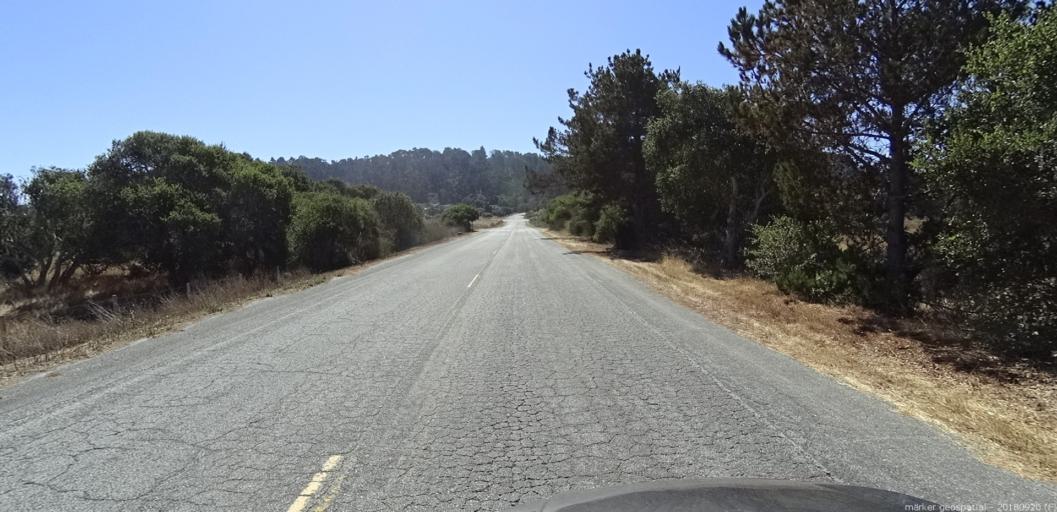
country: US
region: California
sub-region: Monterey County
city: Del Rey Oaks
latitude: 36.5823
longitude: -121.8499
